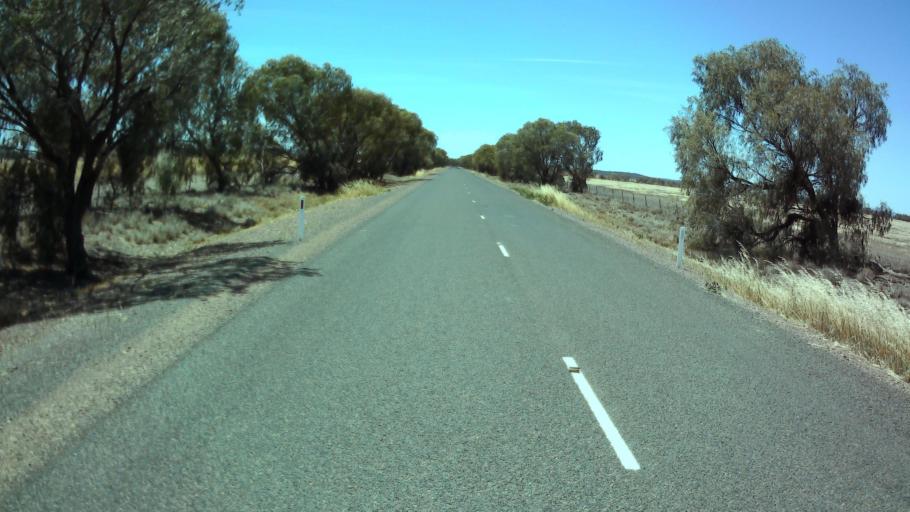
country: AU
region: New South Wales
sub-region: Forbes
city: Forbes
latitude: -33.6618
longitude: 147.6122
